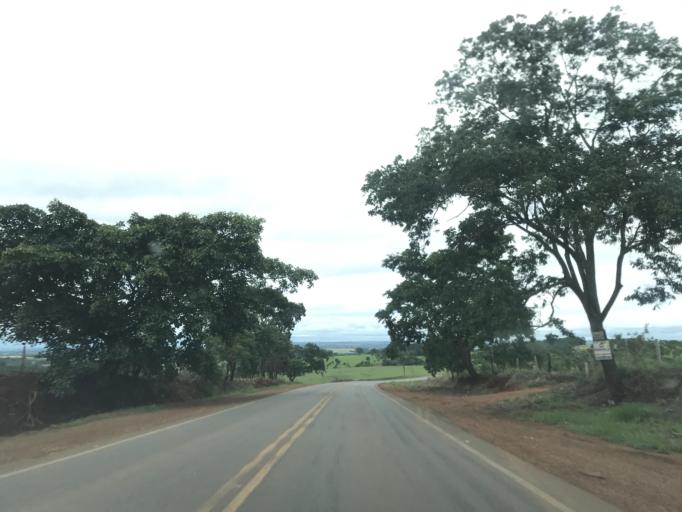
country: BR
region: Goias
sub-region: Vianopolis
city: Vianopolis
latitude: -16.7159
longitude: -48.4046
